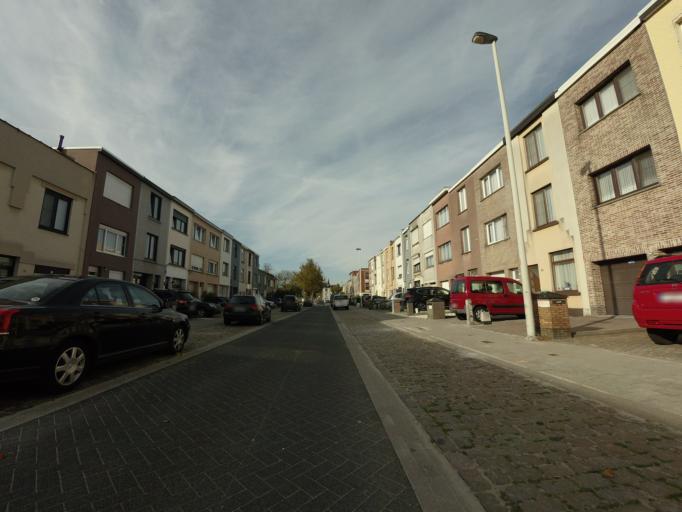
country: BE
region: Flanders
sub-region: Provincie Antwerpen
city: Borsbeek
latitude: 51.2259
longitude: 4.4571
